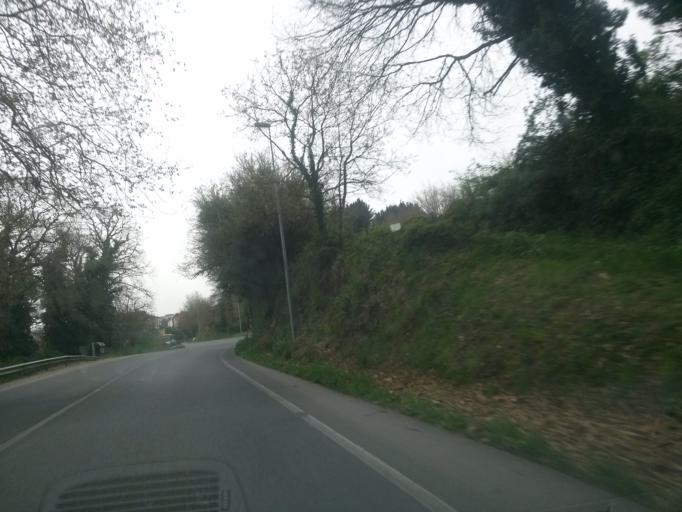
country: ES
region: Galicia
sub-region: Provincia de Lugo
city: Lugo
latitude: 43.0230
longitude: -7.5467
